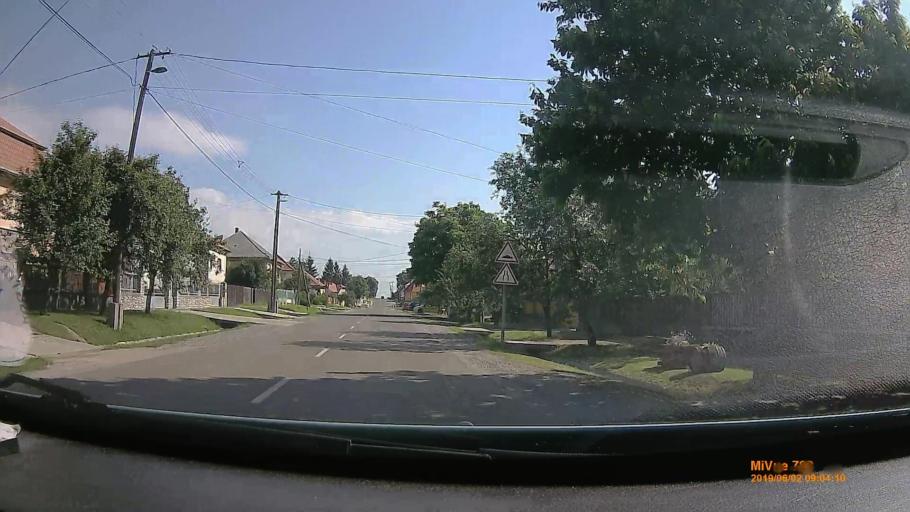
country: HU
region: Borsod-Abauj-Zemplen
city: Kazincbarcika
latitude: 48.1687
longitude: 20.6415
